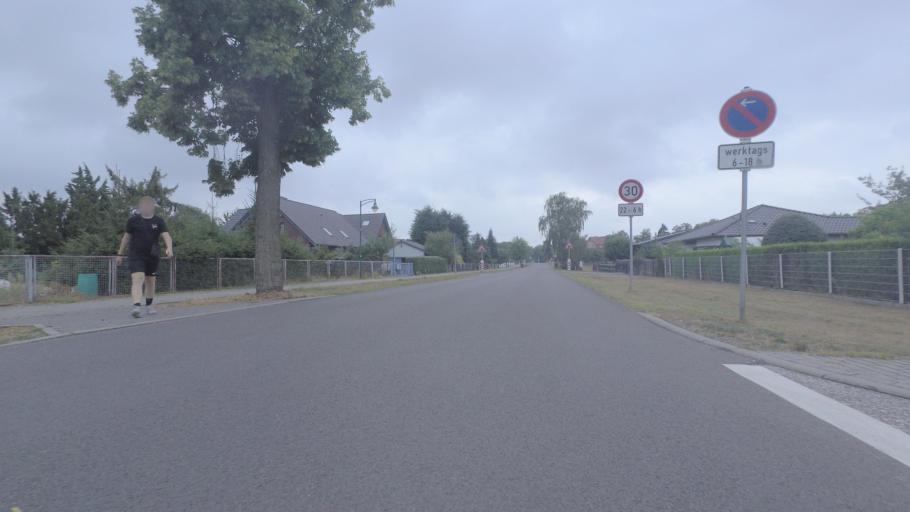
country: DE
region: Brandenburg
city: Wustermark
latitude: 52.5172
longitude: 12.9744
